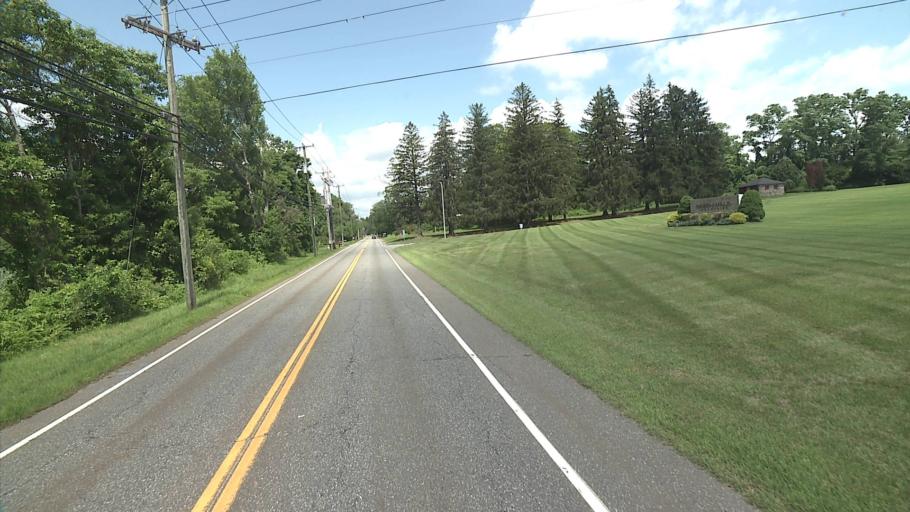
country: US
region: Connecticut
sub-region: Middlesex County
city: Chester Center
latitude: 41.4213
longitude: -72.4455
